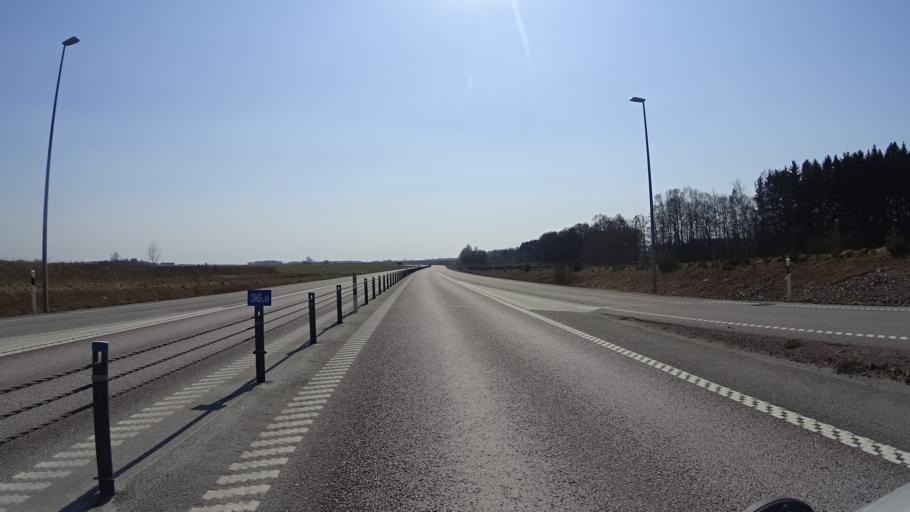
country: SE
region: OEstergoetland
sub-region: Motala Kommun
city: Stenstorp
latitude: 58.4568
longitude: 15.0501
